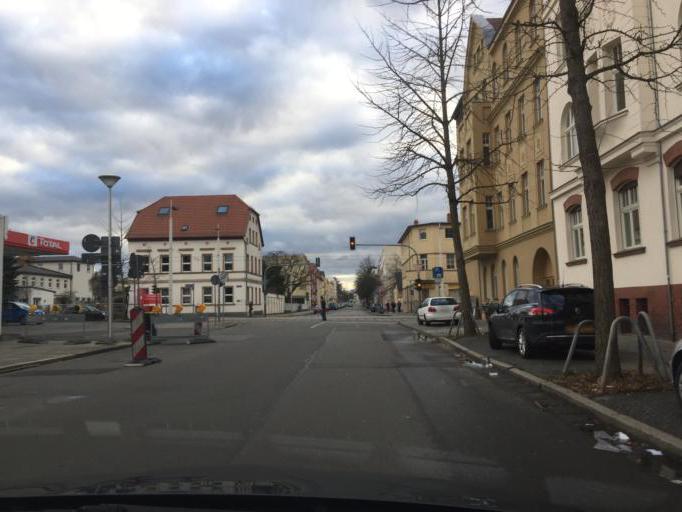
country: DE
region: Brandenburg
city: Cottbus
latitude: 51.7617
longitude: 14.3239
